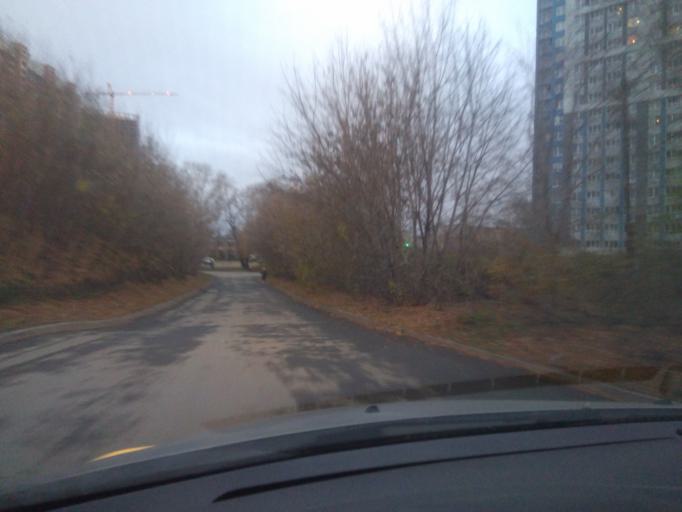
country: RU
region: Sverdlovsk
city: Yekaterinburg
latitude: 56.8549
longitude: 60.5834
